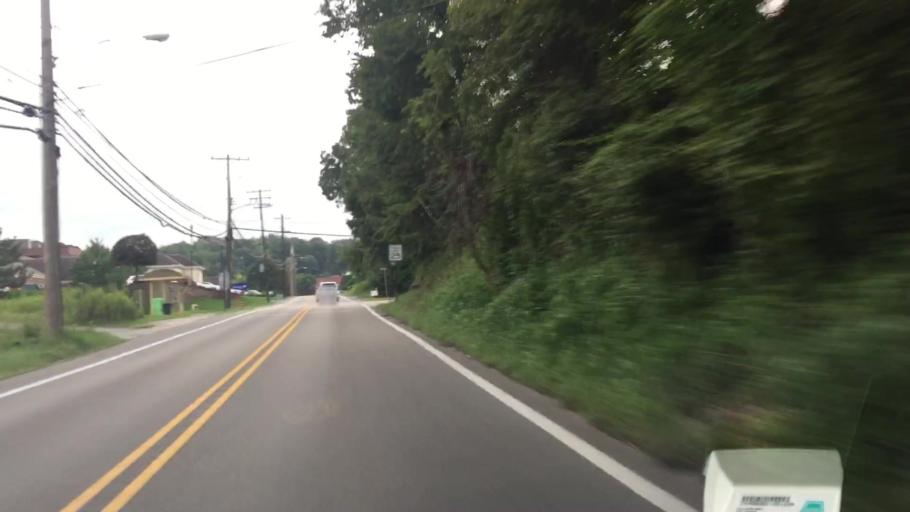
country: US
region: Pennsylvania
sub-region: Allegheny County
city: Whitehall
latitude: 40.3631
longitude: -80.0003
